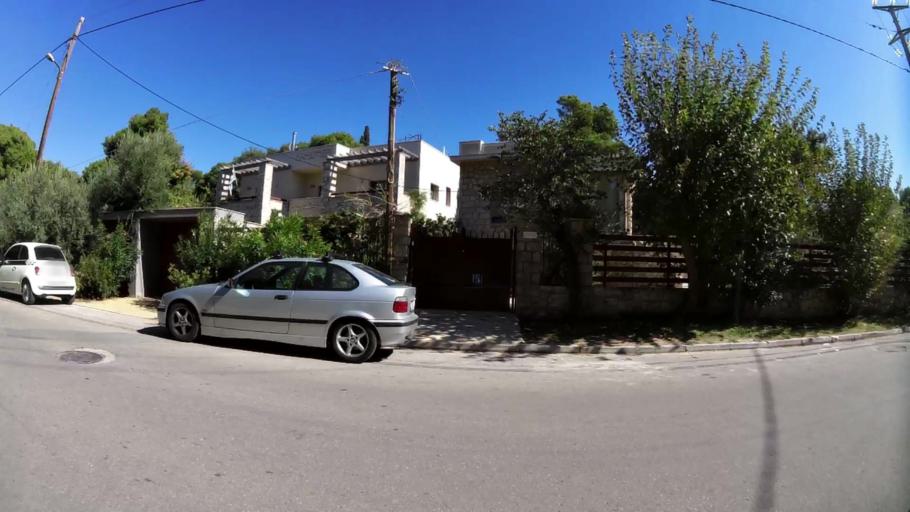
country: GR
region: Attica
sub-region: Nomarchia Athinas
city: Nea Erythraia
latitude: 38.0900
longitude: 23.8019
